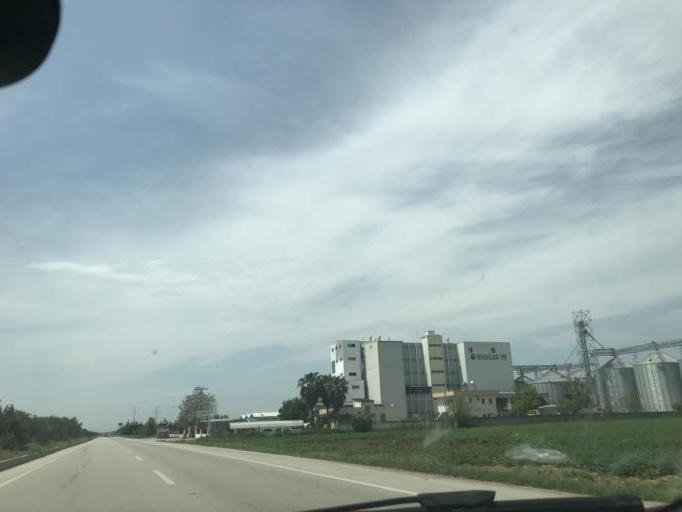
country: TR
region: Adana
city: Yakapinar
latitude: 36.9743
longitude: 35.4978
